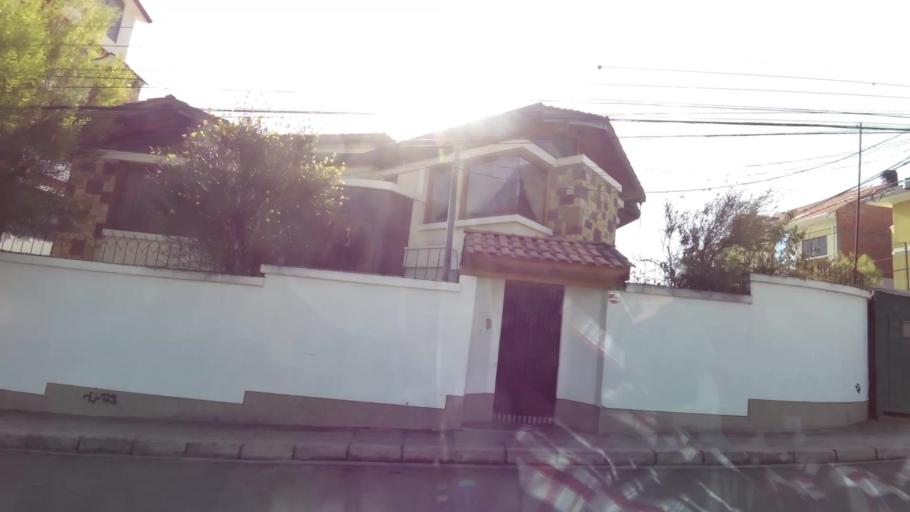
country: BO
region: La Paz
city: La Paz
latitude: -16.5275
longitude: -68.0751
